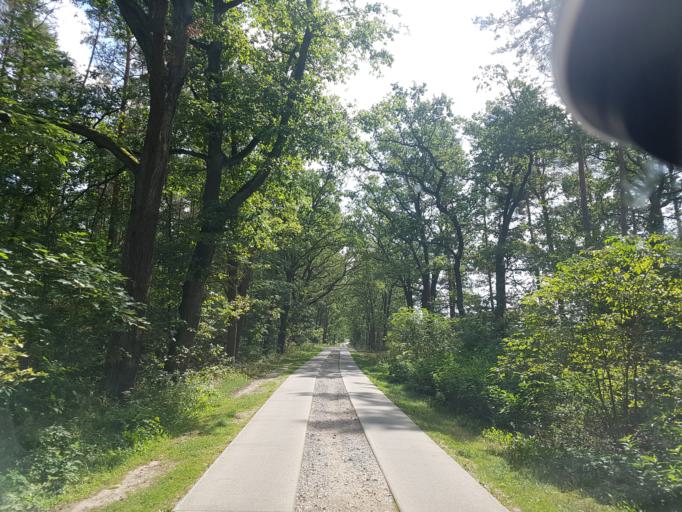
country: DE
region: Brandenburg
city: Borkwalde
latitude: 52.3136
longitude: 12.7781
